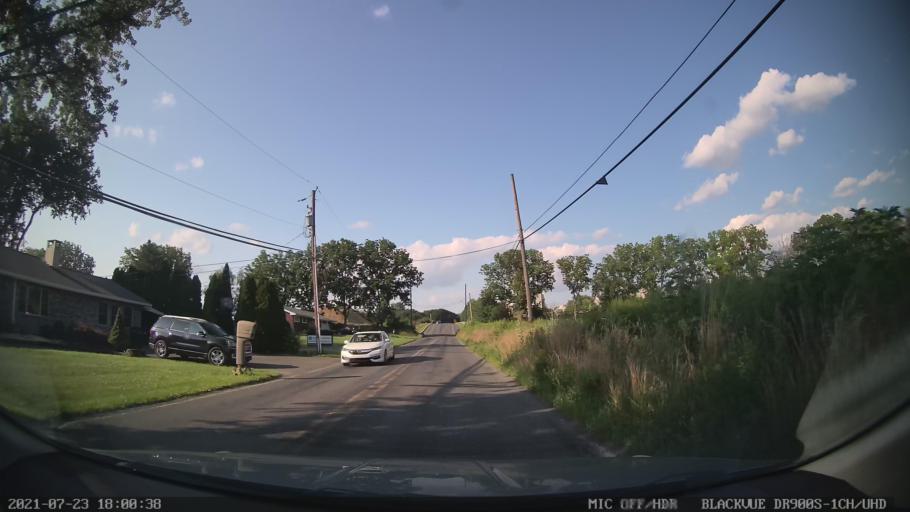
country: US
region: Pennsylvania
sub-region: Lehigh County
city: Emmaus
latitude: 40.5258
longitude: -75.5248
